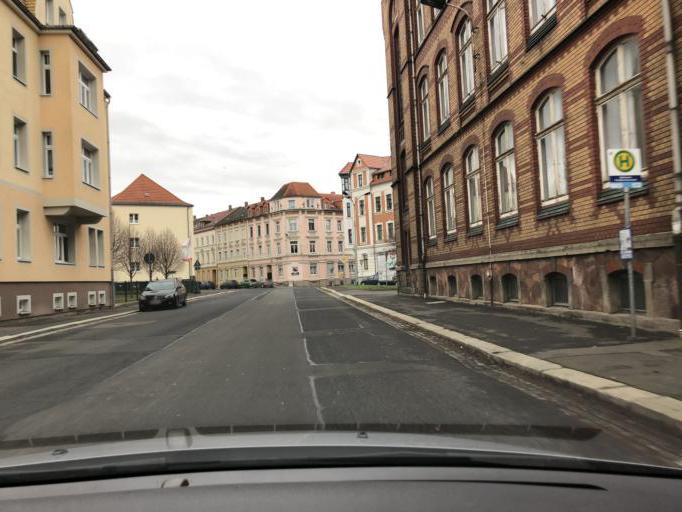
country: DE
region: Saxony
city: Rosswein
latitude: 51.0655
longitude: 13.1770
